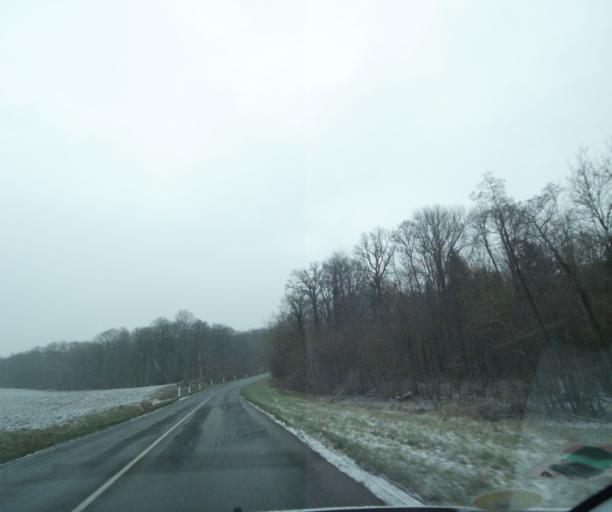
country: FR
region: Champagne-Ardenne
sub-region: Departement de la Haute-Marne
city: Wassy
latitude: 48.4774
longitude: 5.0112
